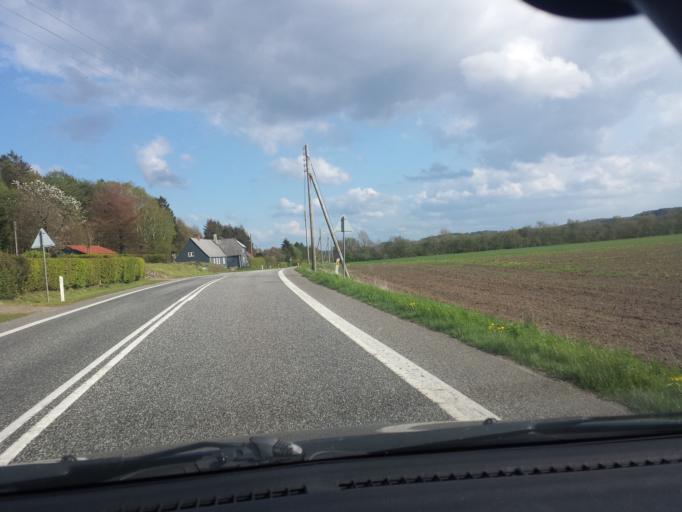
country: DK
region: Central Jutland
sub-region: Favrskov Kommune
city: Ulstrup
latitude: 56.4611
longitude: 9.7433
